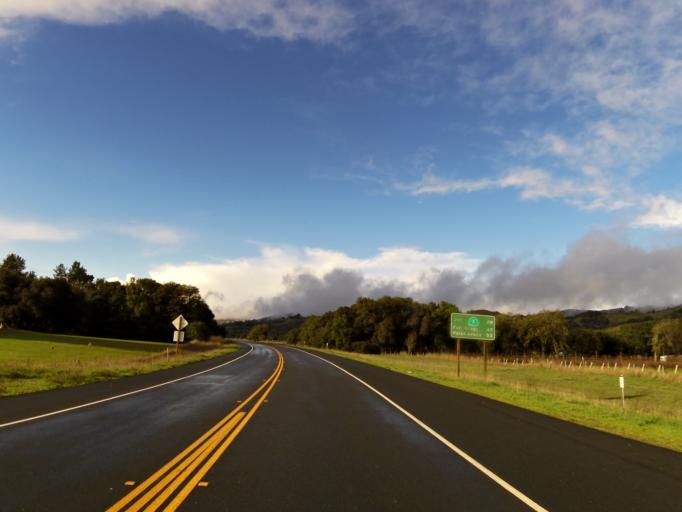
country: US
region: California
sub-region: Mendocino County
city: Boonville
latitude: 39.0188
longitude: -123.3743
